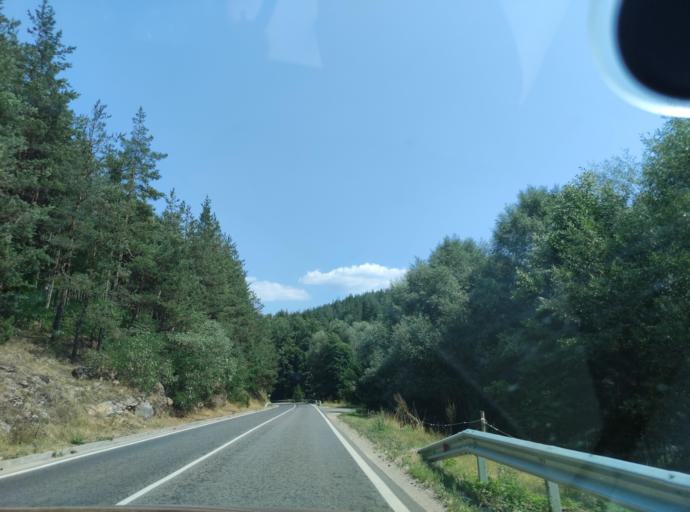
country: BG
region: Blagoevgrad
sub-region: Obshtina Razlog
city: Razlog
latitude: 41.8877
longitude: 23.5309
